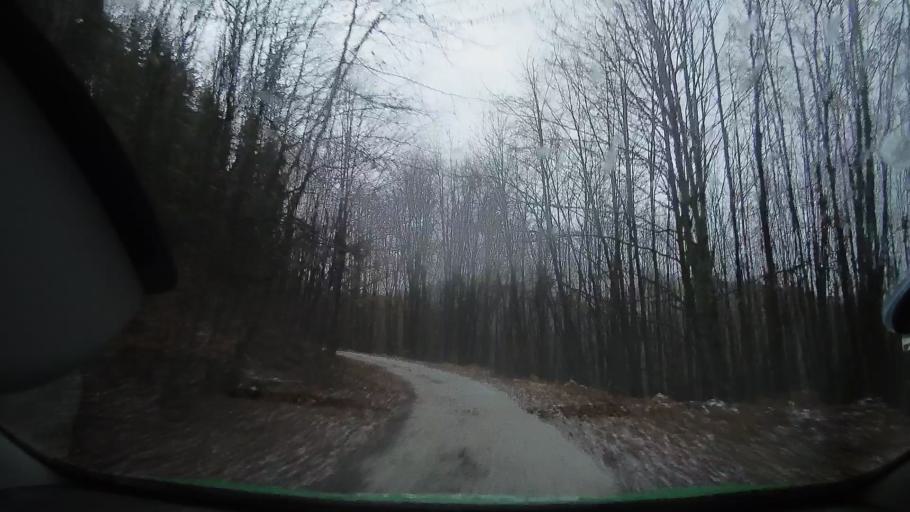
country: RO
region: Alba
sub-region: Comuna Avram Iancu
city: Avram Iancu
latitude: 46.3122
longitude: 22.7952
